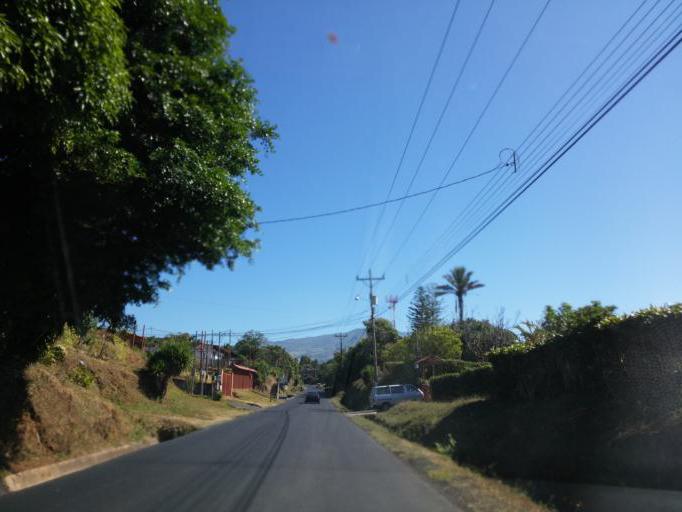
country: CR
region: Alajuela
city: Sabanilla
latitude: 10.0653
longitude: -84.1954
